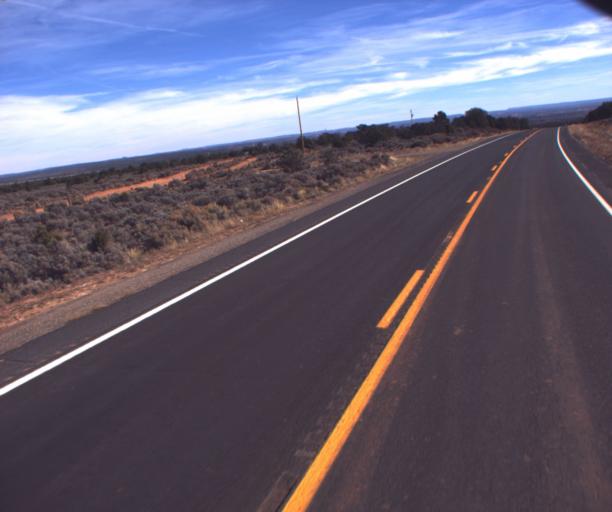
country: US
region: Arizona
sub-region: Coconino County
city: Kaibito
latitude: 36.5835
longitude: -110.8339
